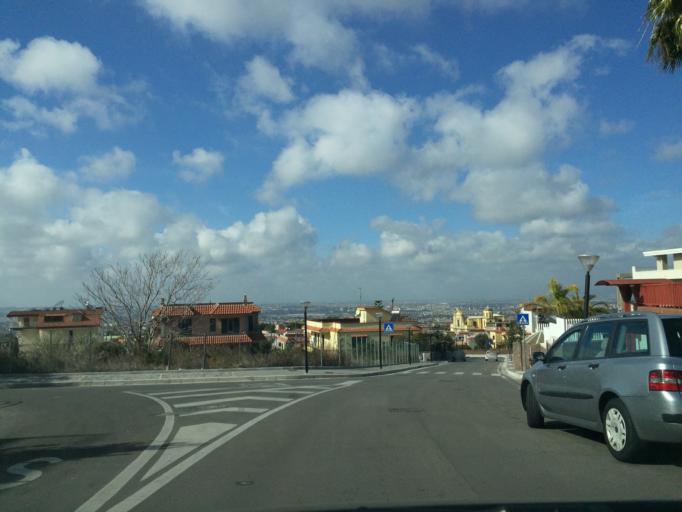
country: IT
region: Campania
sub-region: Provincia di Napoli
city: Pollena Trocchia
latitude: 40.8520
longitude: 14.3814
